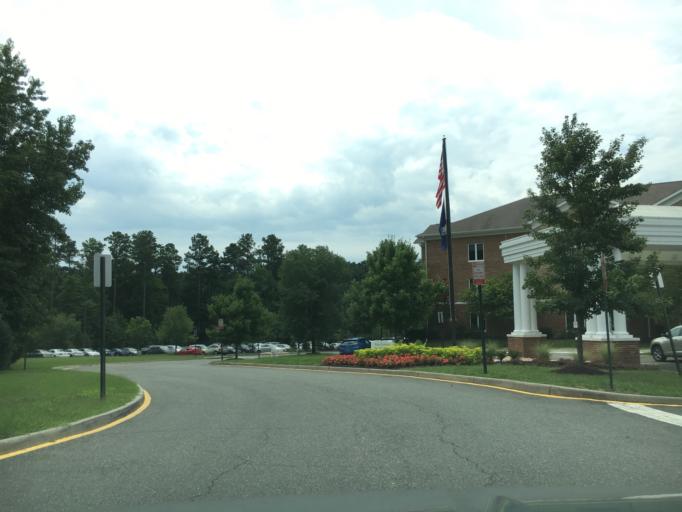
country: US
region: Virginia
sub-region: Henrico County
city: Short Pump
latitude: 37.6081
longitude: -77.6319
